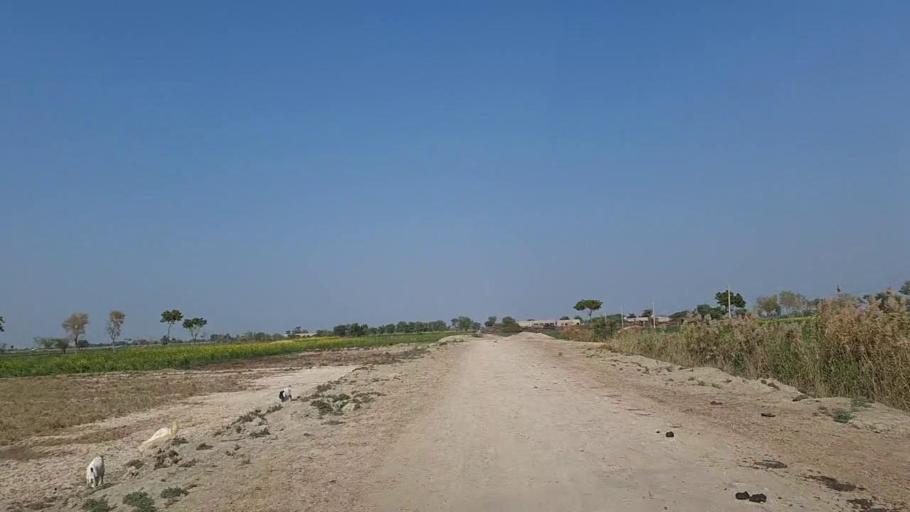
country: PK
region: Sindh
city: Nawabshah
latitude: 26.2924
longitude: 68.5138
